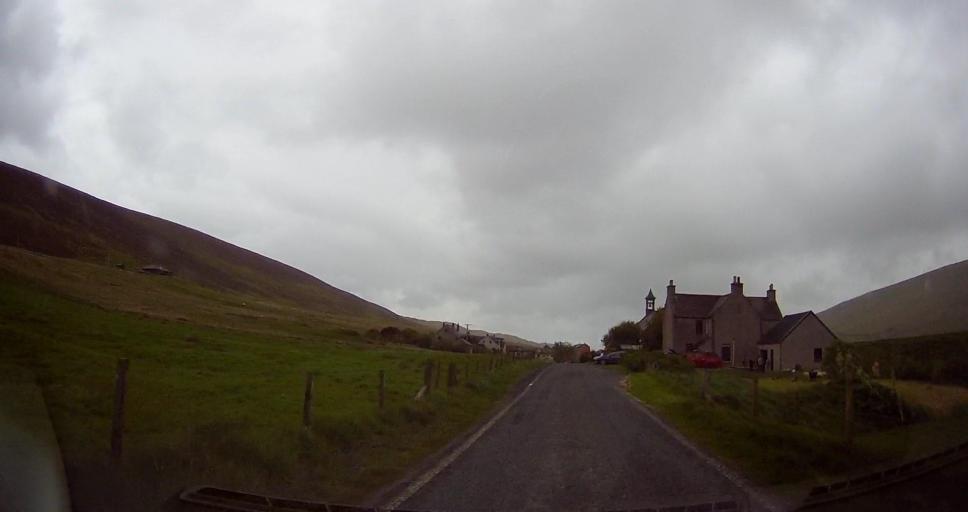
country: GB
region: Scotland
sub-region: Shetland Islands
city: Lerwick
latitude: 60.2567
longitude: -1.2890
